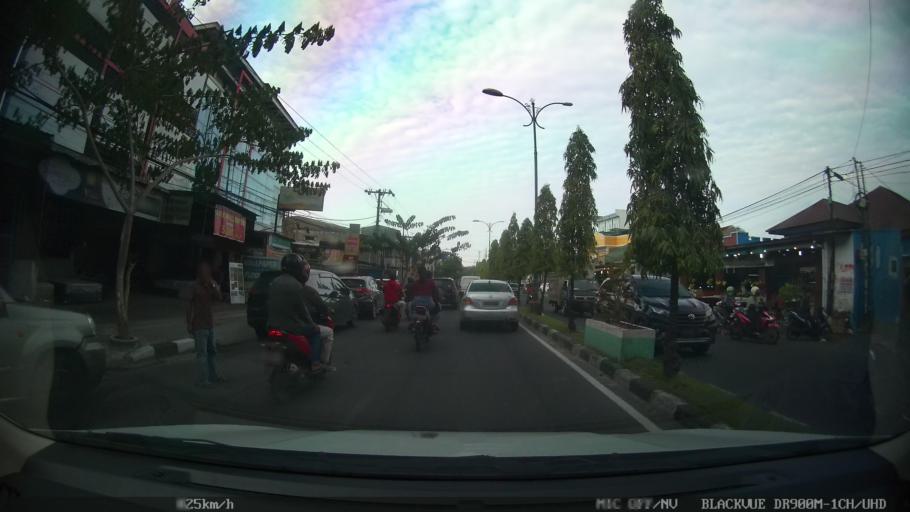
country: ID
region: North Sumatra
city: Sunggal
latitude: 3.5605
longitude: 98.6366
